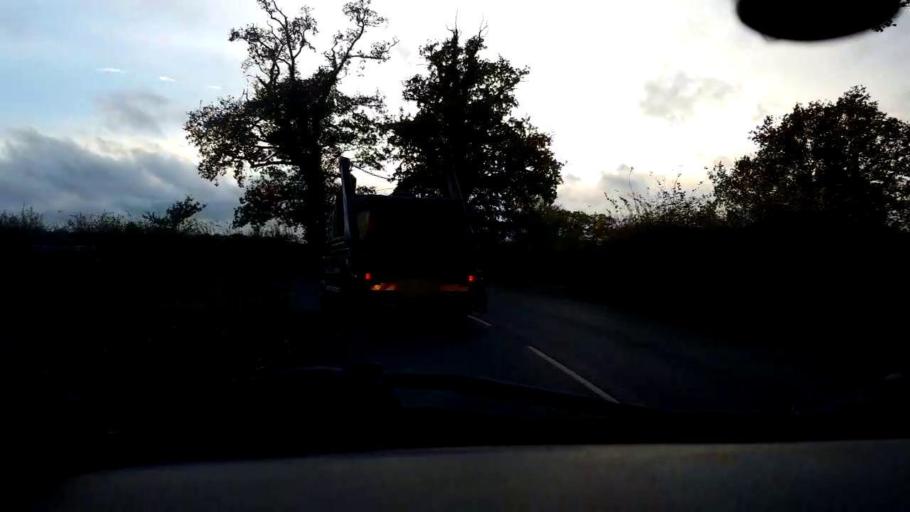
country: GB
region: England
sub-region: Norfolk
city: Mattishall
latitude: 52.6964
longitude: 1.0903
